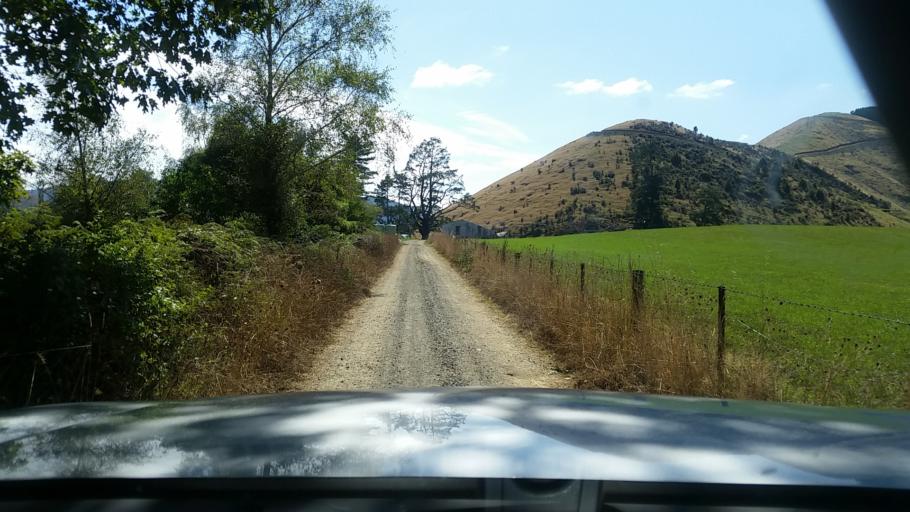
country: NZ
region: Nelson
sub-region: Nelson City
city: Nelson
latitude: -41.2485
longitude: 173.5853
